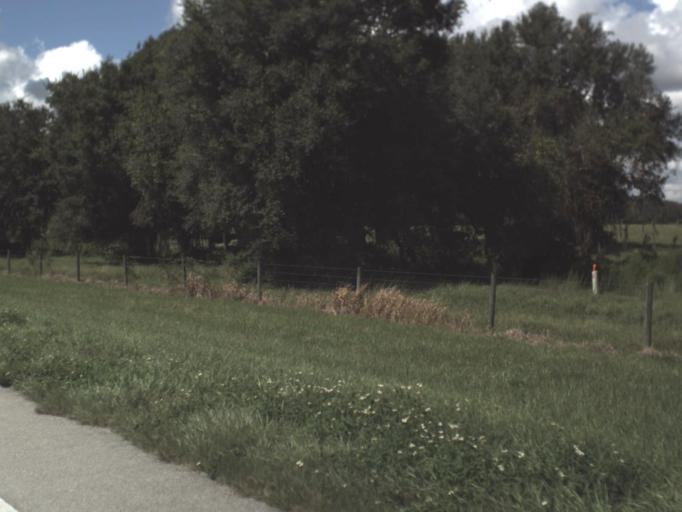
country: US
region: Florida
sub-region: DeSoto County
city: Arcadia
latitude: 27.2533
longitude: -81.9630
